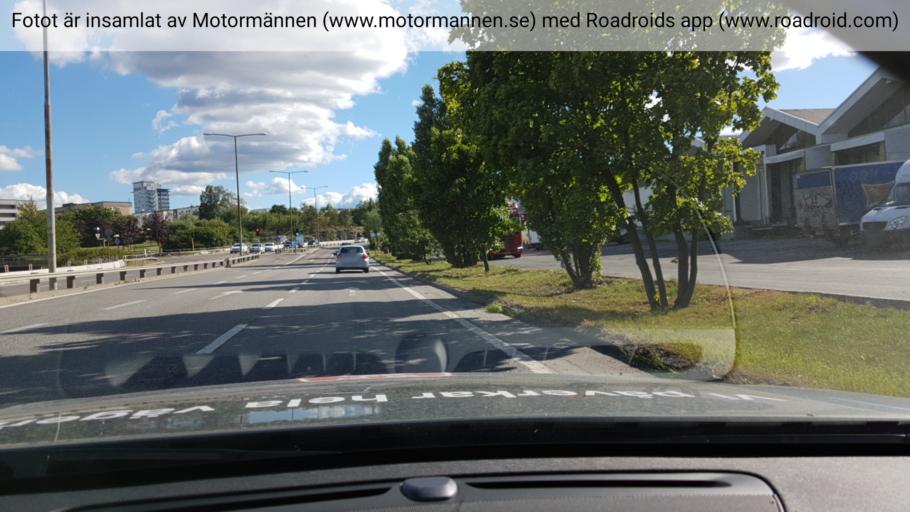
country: SE
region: Stockholm
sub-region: Stockholms Kommun
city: Arsta
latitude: 59.2938
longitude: 18.0341
